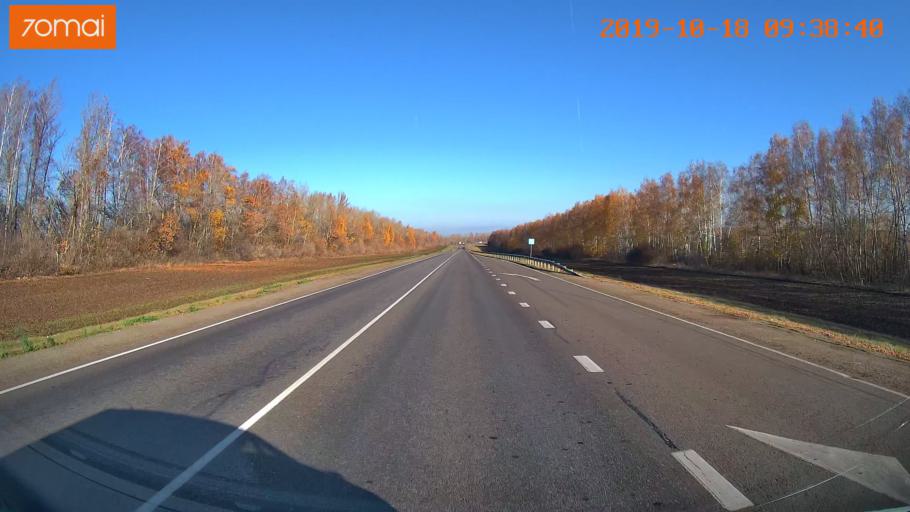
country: RU
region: Tula
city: Yefremov
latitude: 53.2414
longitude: 38.1362
